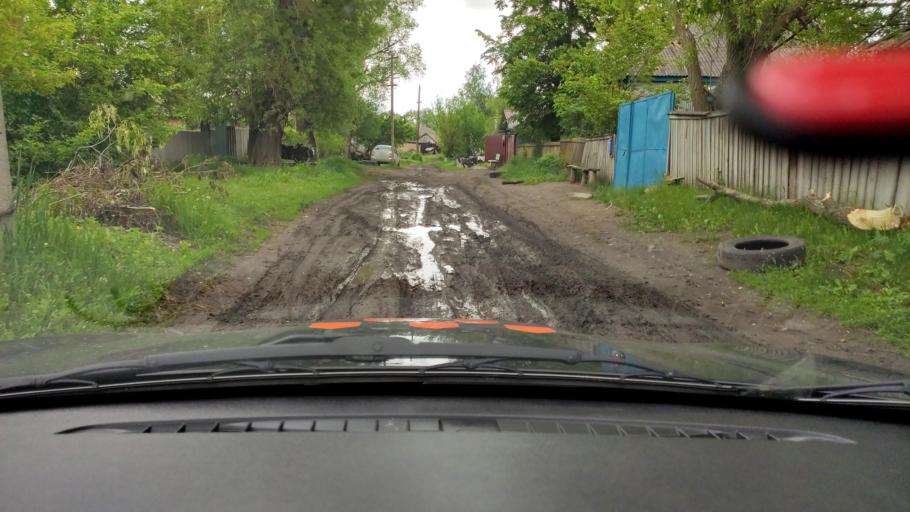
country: RU
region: Voronezj
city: Uryv-Pokrovka
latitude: 51.1061
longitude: 39.1555
